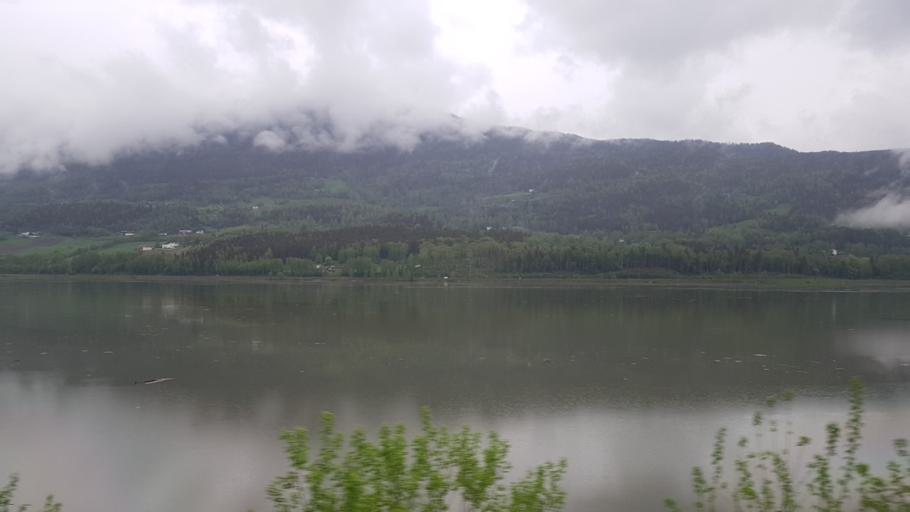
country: NO
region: Oppland
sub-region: Oyer
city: Tretten
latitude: 61.4125
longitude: 10.2370
